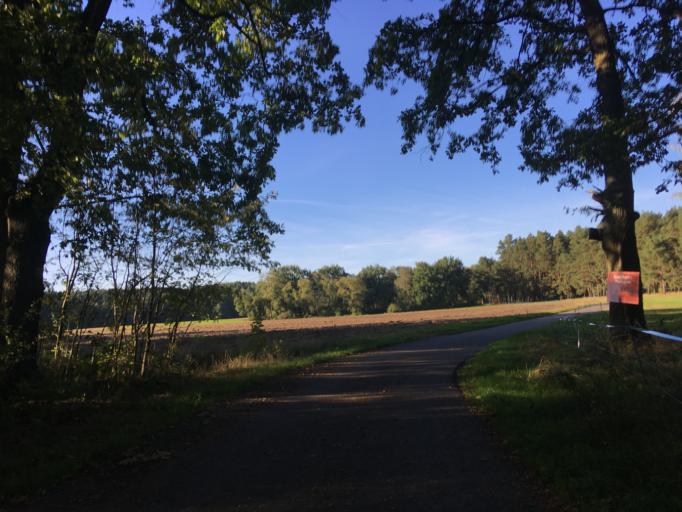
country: PL
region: Lubusz
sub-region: Powiat zarski
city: Trzebiel
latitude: 51.6040
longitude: 14.7603
